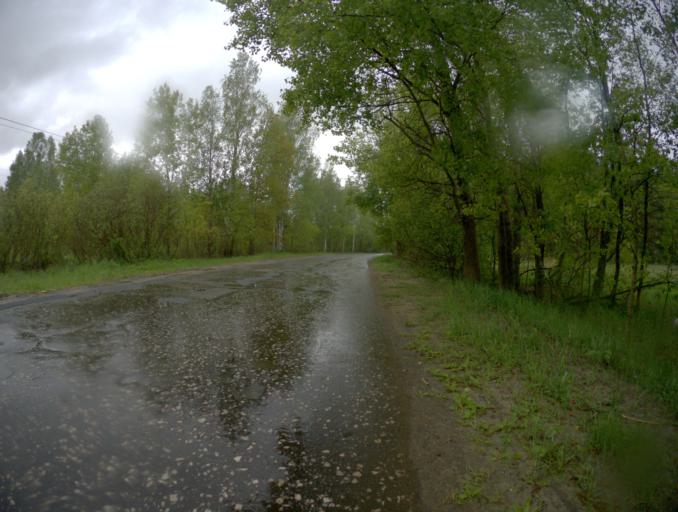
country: RU
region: Vladimir
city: Velikodvorskiy
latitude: 55.3712
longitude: 40.8308
